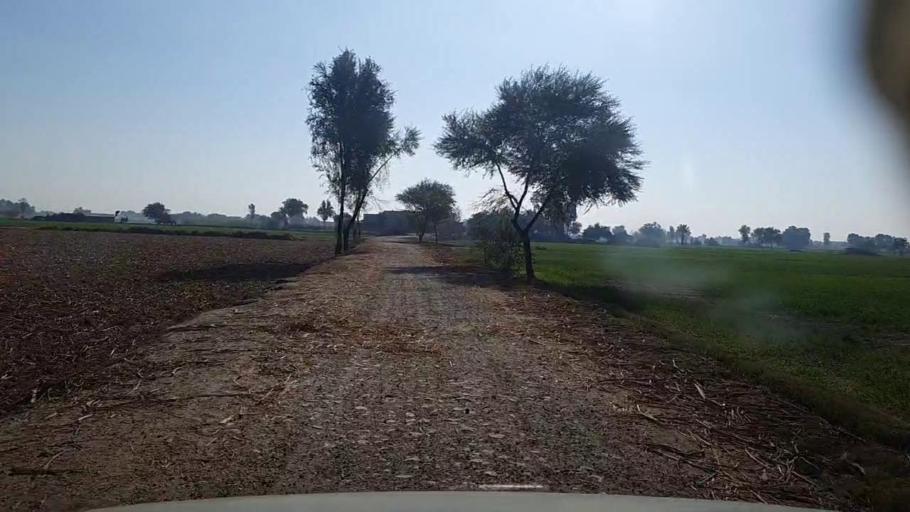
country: PK
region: Sindh
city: Khairpur
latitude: 28.0558
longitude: 69.7377
